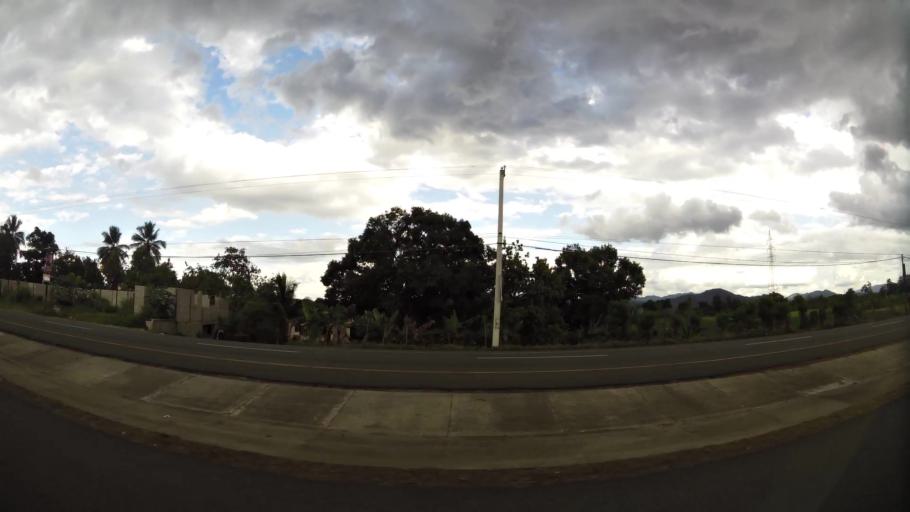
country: DO
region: Monsenor Nouel
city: Sabana del Puerto
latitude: 19.0475
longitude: -70.4458
